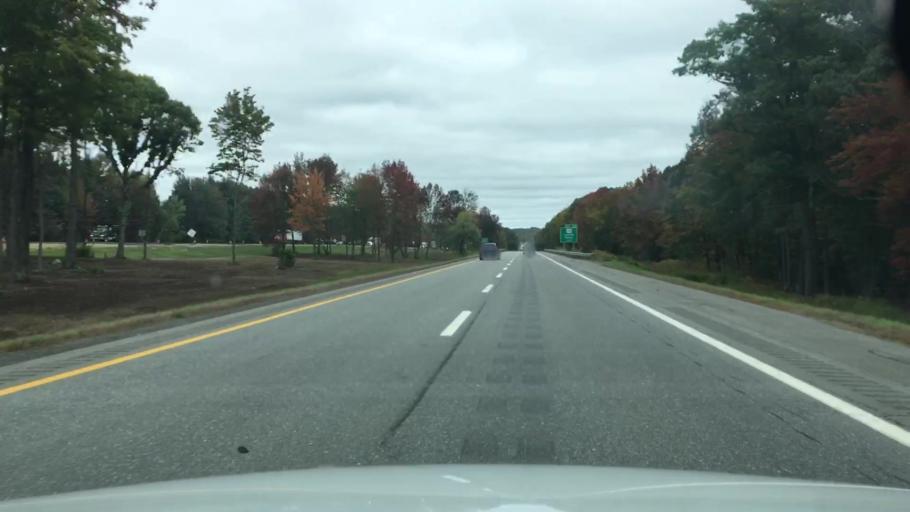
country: US
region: Maine
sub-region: Kennebec County
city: Waterville
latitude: 44.5790
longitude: -69.6281
